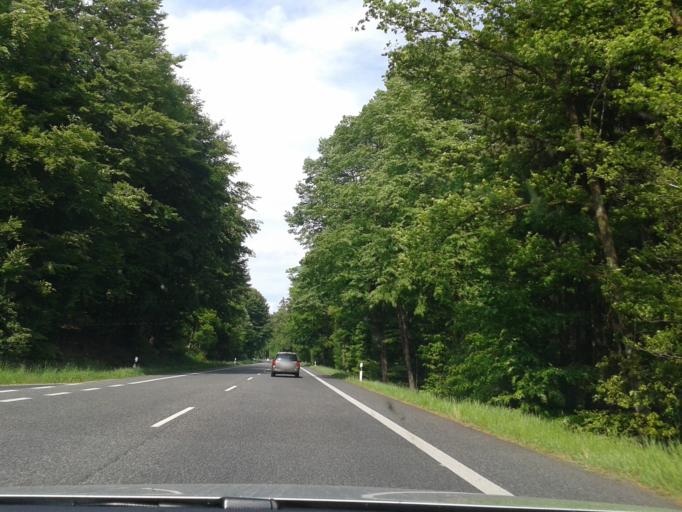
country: DE
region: Hesse
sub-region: Regierungsbezirk Giessen
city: Munchhausen
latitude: 50.9946
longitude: 8.7620
